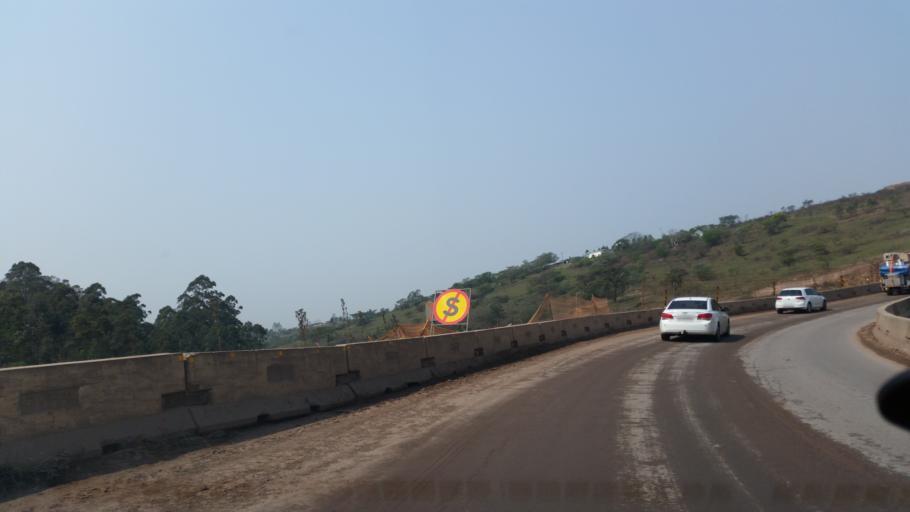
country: ZA
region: KwaZulu-Natal
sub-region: eThekwini Metropolitan Municipality
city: Mpumalanga
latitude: -29.7567
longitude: 30.6671
